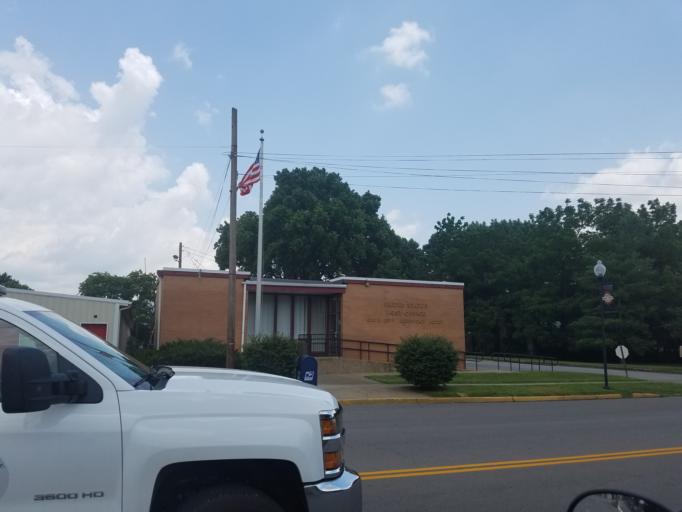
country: US
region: Kentucky
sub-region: Barren County
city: Cave City
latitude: 37.1375
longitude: -85.9580
